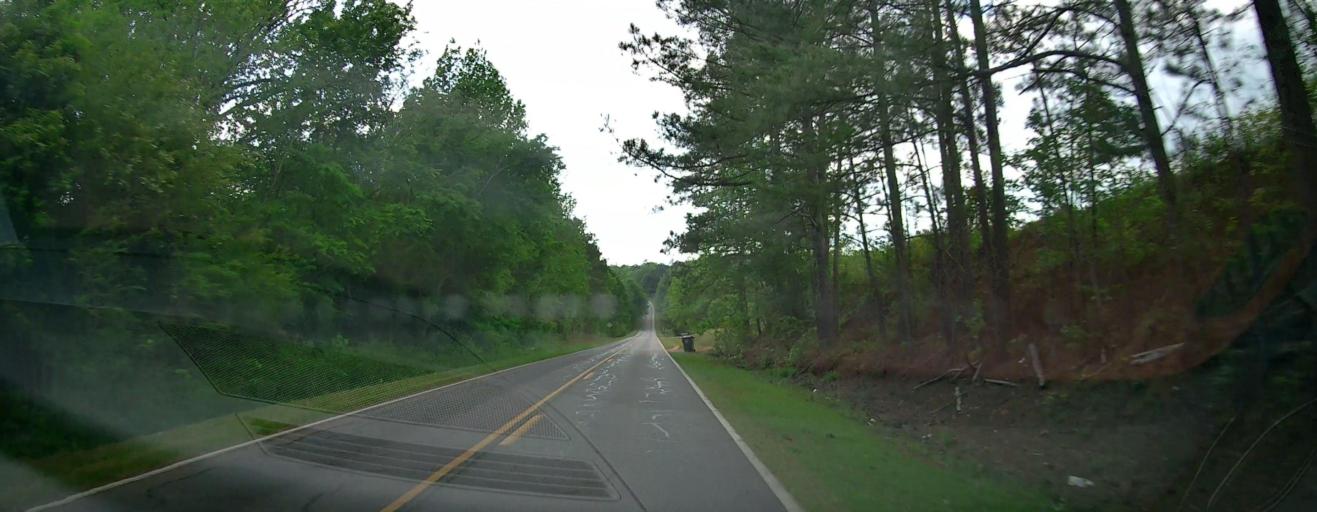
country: US
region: Georgia
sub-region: Baldwin County
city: Hardwick
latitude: 33.0623
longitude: -83.1425
